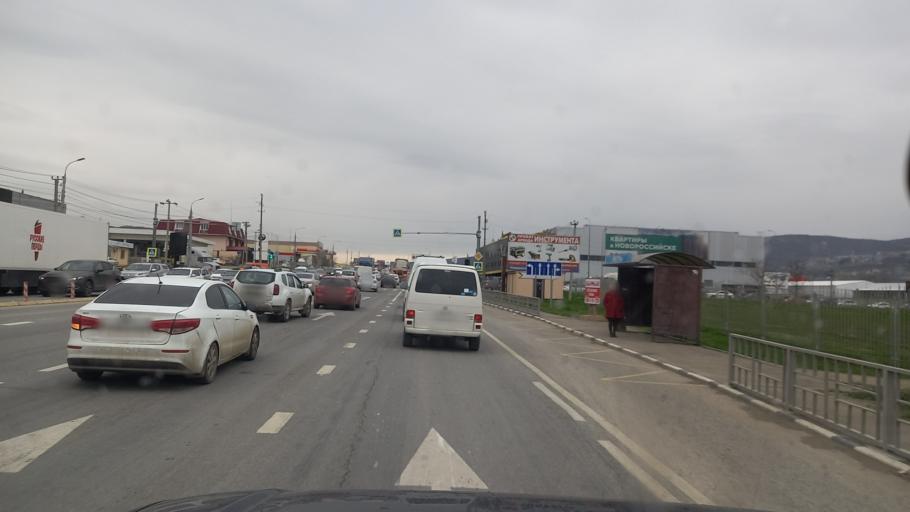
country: RU
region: Krasnodarskiy
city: Gayduk
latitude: 44.7713
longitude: 37.6968
